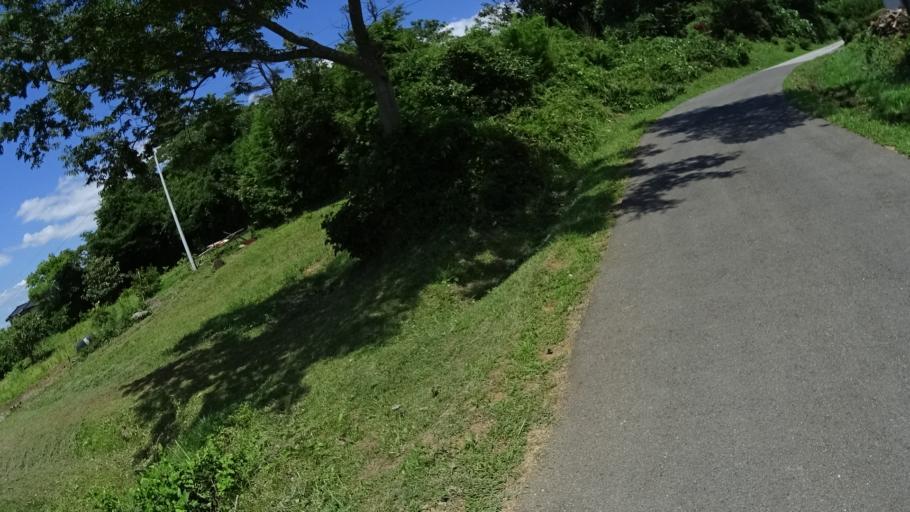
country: JP
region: Iwate
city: Ofunato
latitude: 38.8367
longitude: 141.6241
